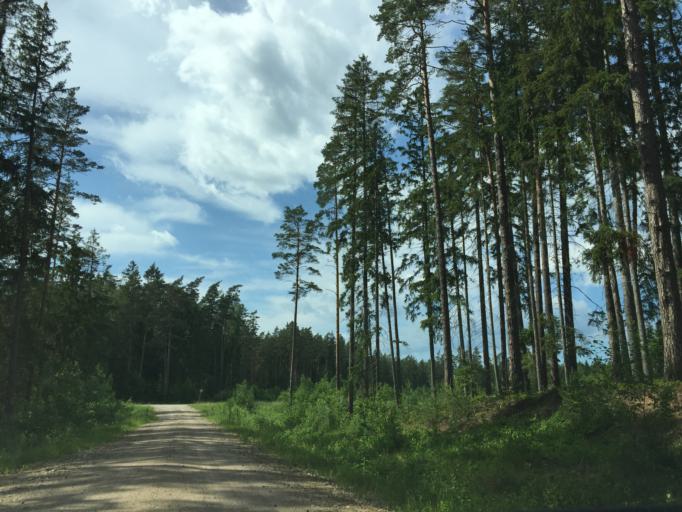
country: LV
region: Tukuma Rajons
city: Tukums
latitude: 57.0170
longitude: 23.2470
